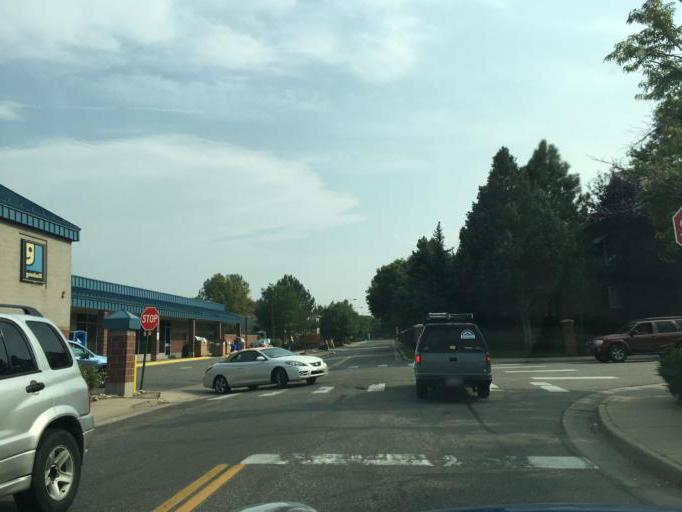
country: US
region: Colorado
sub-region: Arapahoe County
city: Glendale
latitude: 39.7077
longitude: -104.9296
